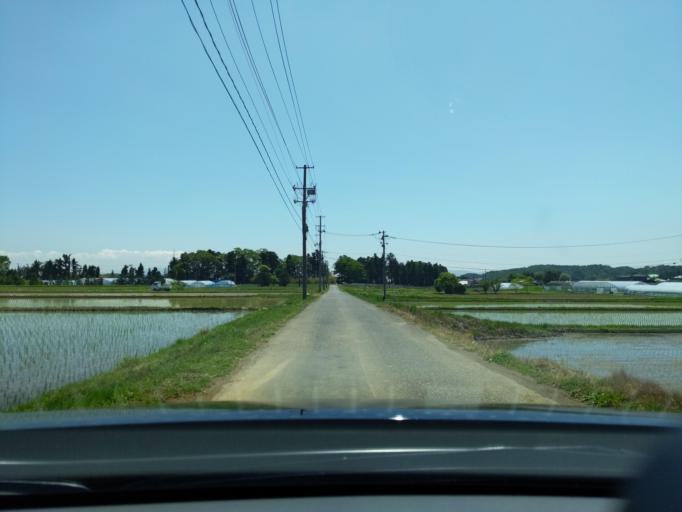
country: JP
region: Fukushima
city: Koriyama
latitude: 37.4000
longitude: 140.2651
